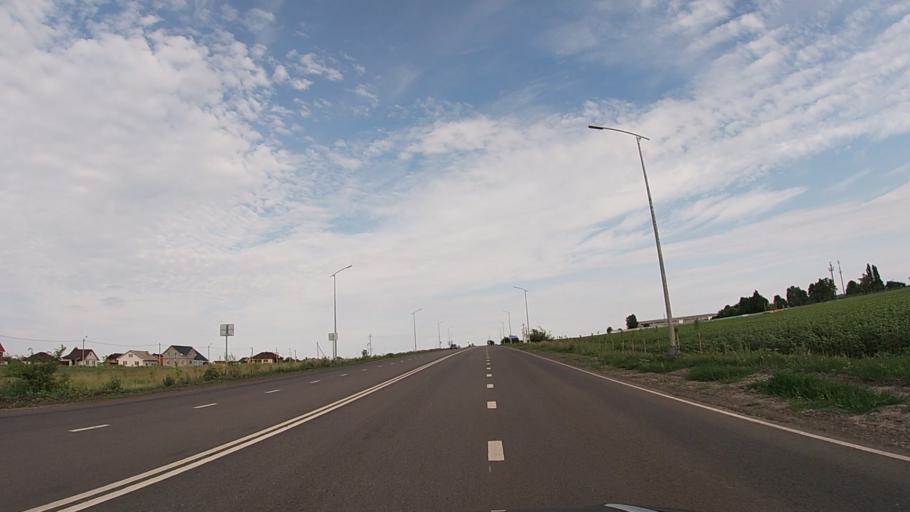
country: RU
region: Belgorod
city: Severnyy
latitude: 50.6720
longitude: 36.4806
